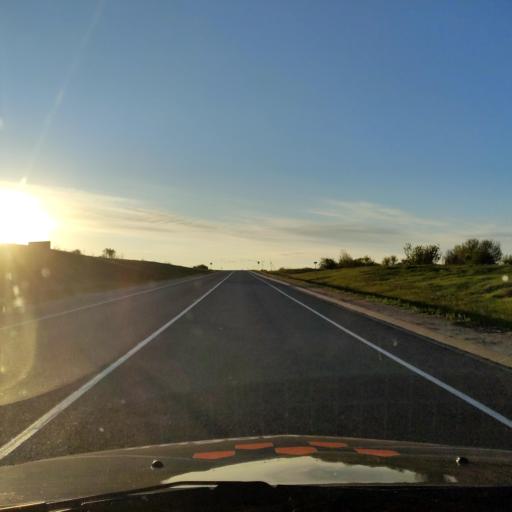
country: RU
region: Orjol
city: Livny
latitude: 52.4493
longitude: 37.6152
